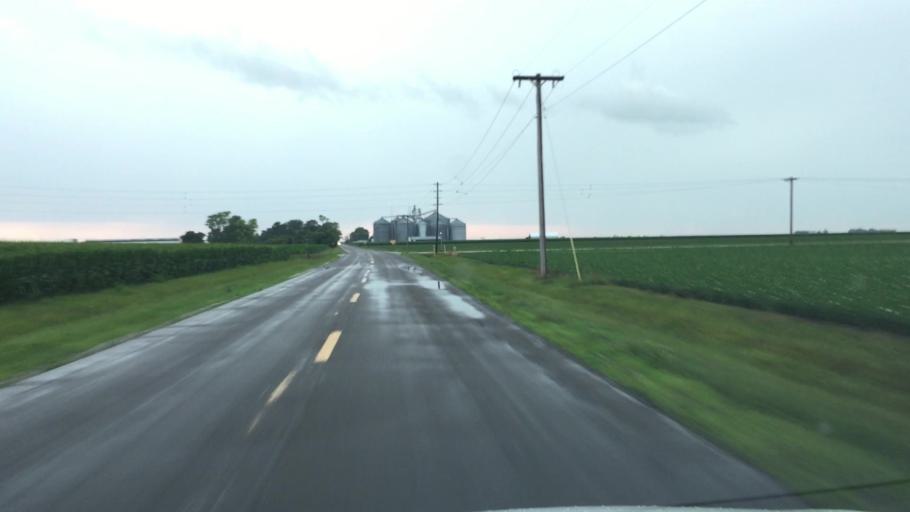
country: US
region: Illinois
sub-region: Hancock County
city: Carthage
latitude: 40.5206
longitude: -91.1563
